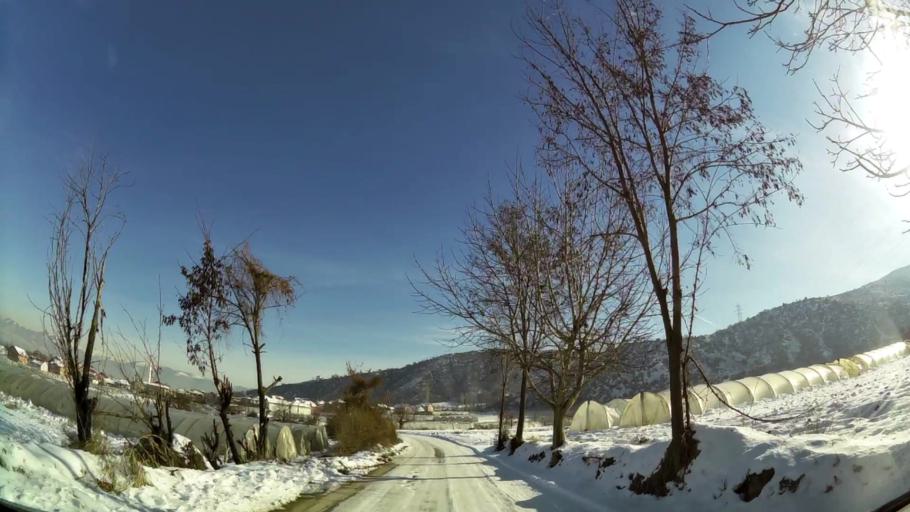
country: MK
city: Grchec
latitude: 41.9912
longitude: 21.3374
